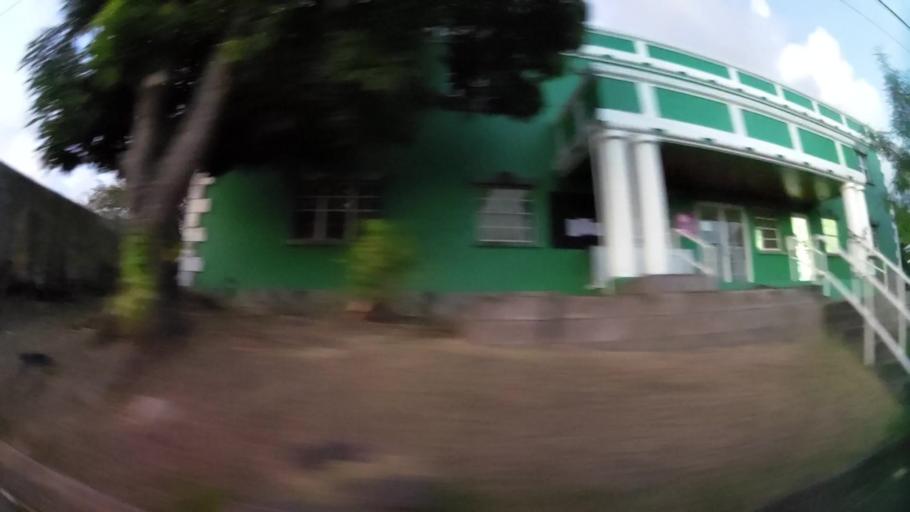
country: KN
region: Saint Thomas Middle Island
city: Middle Island
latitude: 17.3224
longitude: -62.8039
